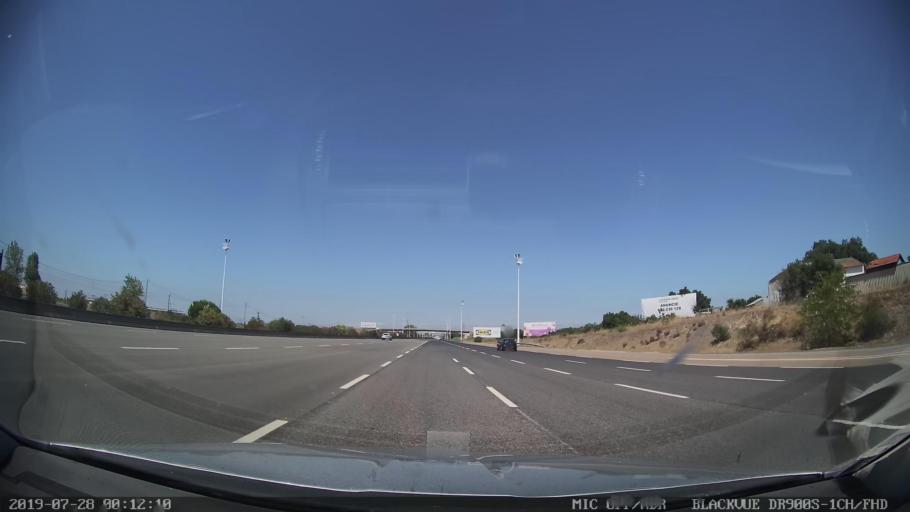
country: PT
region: Setubal
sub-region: Montijo
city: Montijo
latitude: 38.7216
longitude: -8.9608
